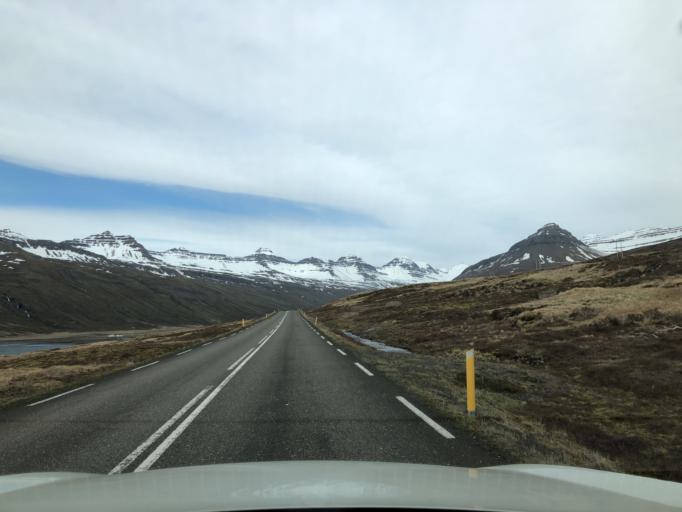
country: IS
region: East
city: Eskifjoerdur
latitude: 64.8408
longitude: -13.9257
